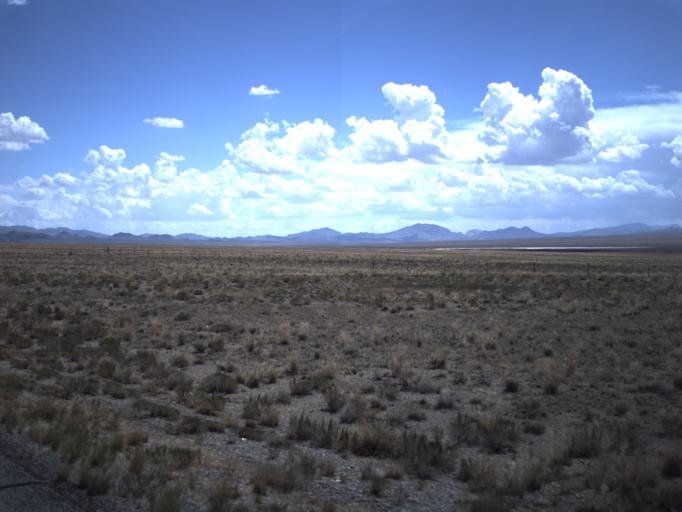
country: US
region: Nevada
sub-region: White Pine County
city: McGill
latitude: 39.0425
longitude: -113.8585
